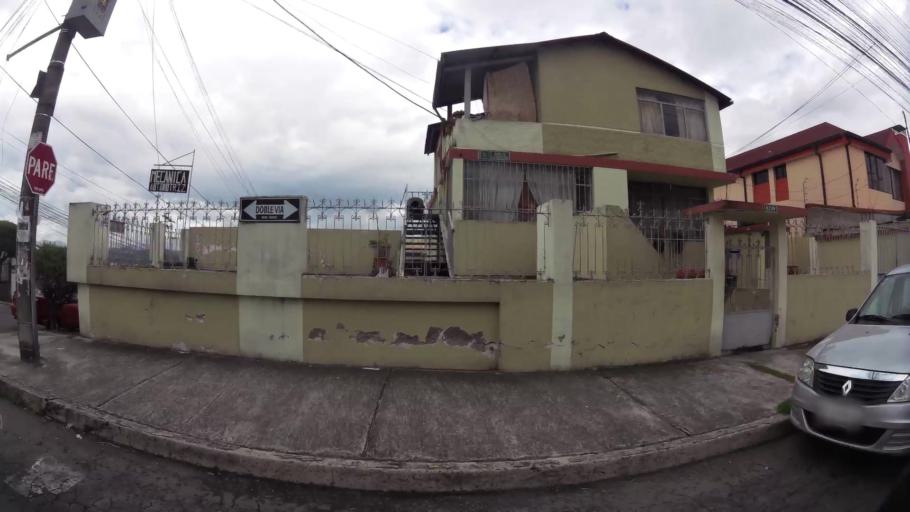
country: EC
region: Pichincha
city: Quito
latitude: -0.1863
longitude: -78.5022
